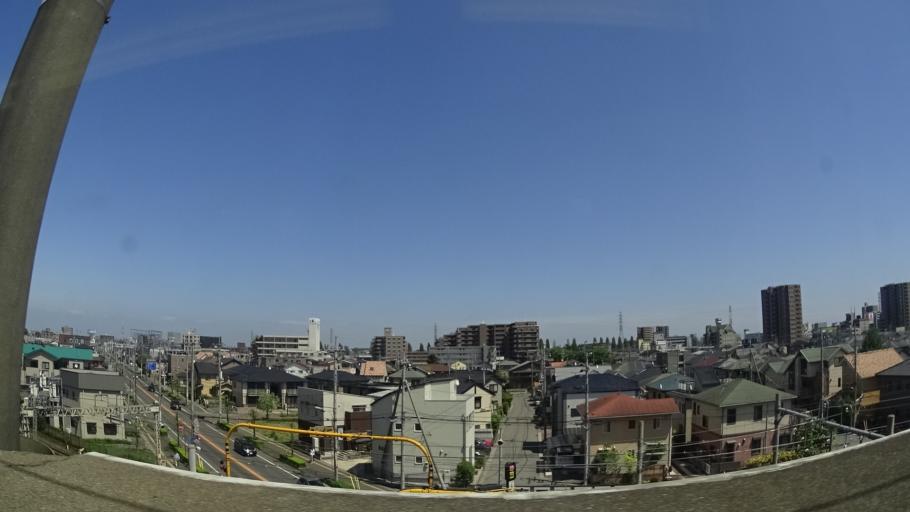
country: JP
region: Tochigi
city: Utsunomiya-shi
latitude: 36.5675
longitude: 139.9003
